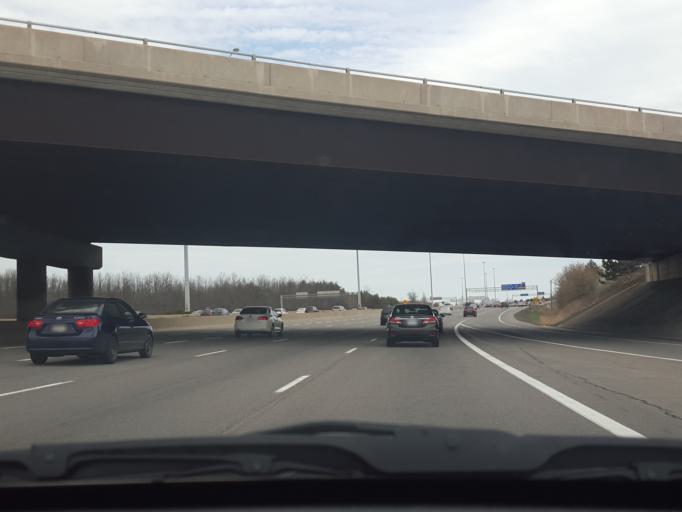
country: CA
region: Ontario
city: Scarborough
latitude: 43.7992
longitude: -79.1669
